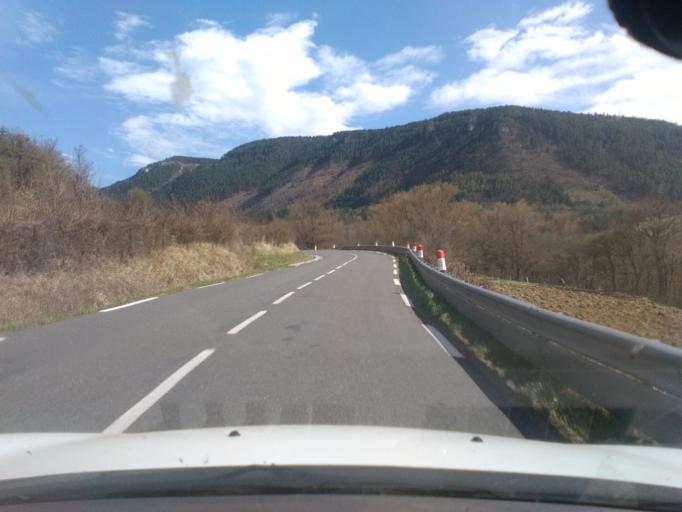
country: FR
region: Languedoc-Roussillon
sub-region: Departement de la Lozere
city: Mende
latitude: 44.4603
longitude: 3.5211
